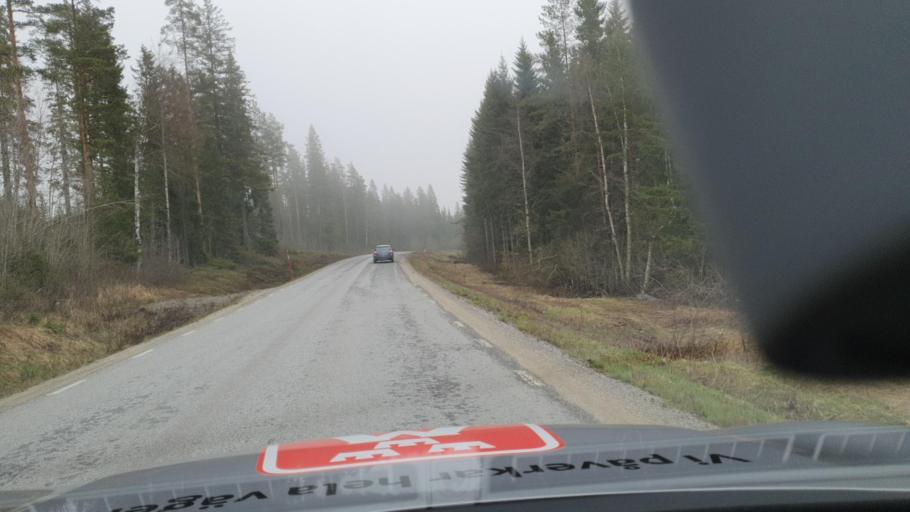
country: SE
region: Vaesternorrland
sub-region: OErnskoeldsviks Kommun
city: Husum
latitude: 63.4845
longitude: 19.1999
